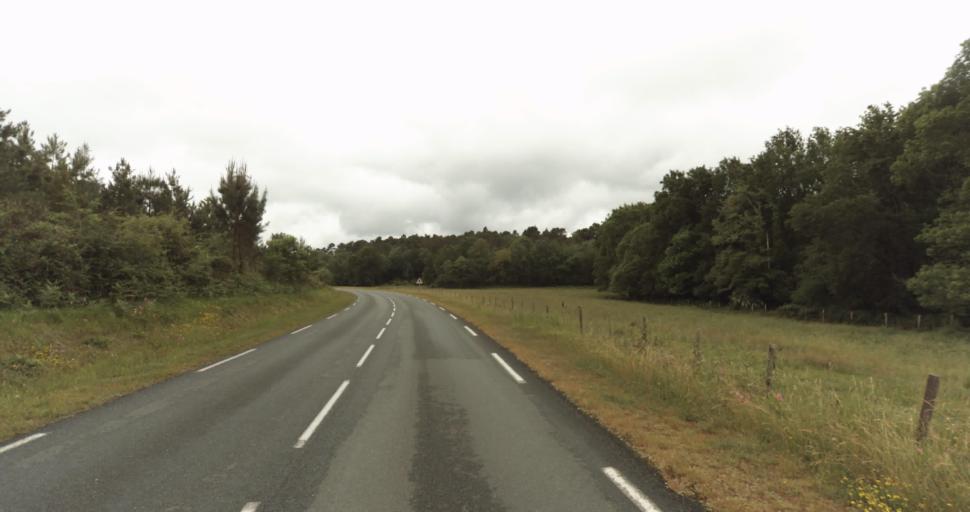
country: FR
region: Aquitaine
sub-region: Departement de la Dordogne
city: Belves
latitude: 44.6850
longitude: 0.9897
